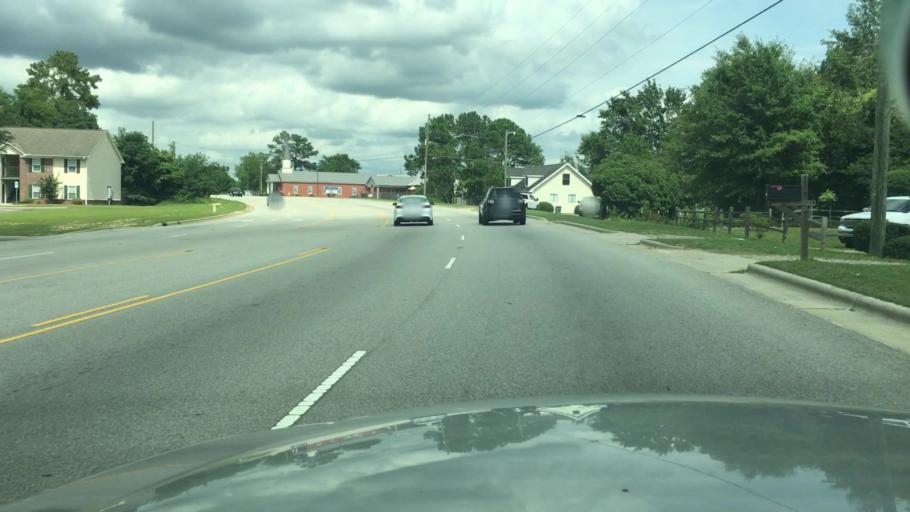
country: US
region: North Carolina
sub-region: Cumberland County
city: Hope Mills
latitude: 35.0020
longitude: -78.9731
